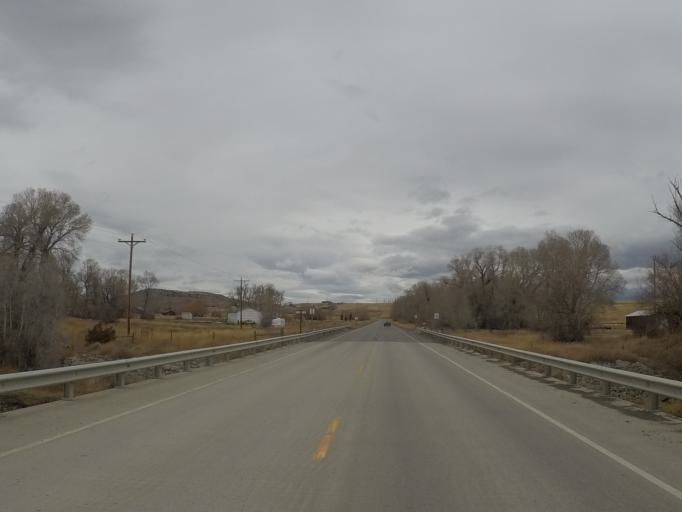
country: US
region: Montana
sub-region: Sweet Grass County
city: Big Timber
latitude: 45.8579
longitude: -109.9394
